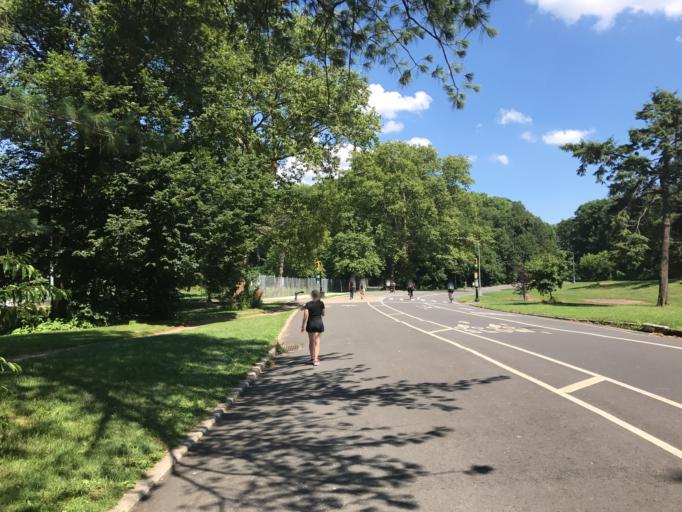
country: US
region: New York
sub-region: Kings County
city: Brooklyn
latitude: 40.6602
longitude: -73.9763
